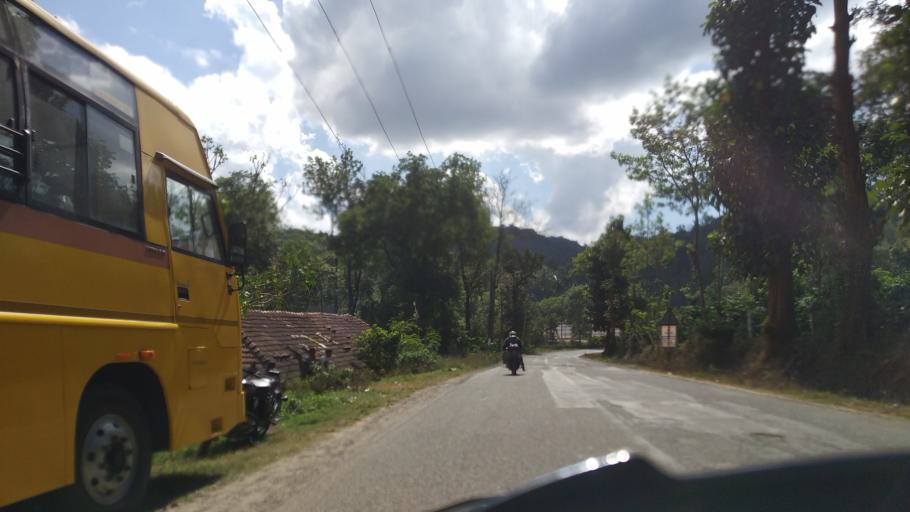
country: IN
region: Karnataka
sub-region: Kodagu
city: Ponnampet
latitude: 11.9654
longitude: 76.0571
